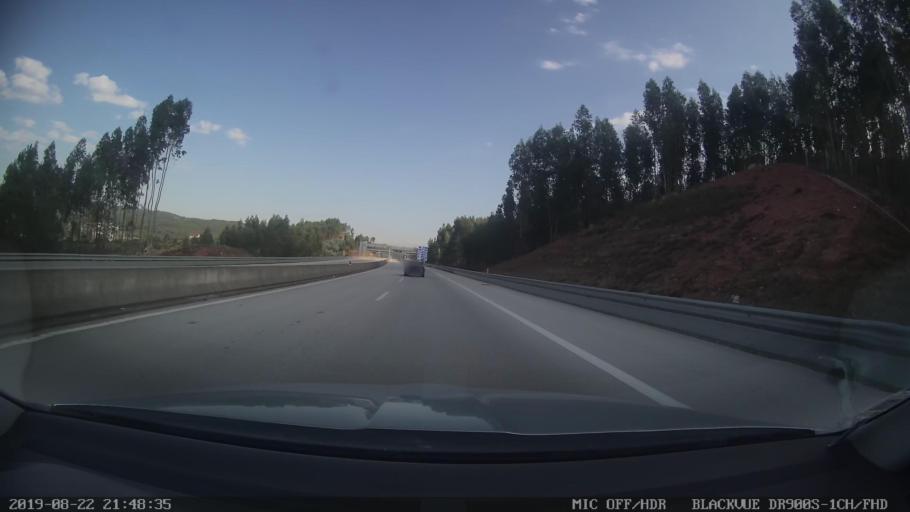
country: PT
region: Coimbra
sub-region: Penela
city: Penela
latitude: 40.0283
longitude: -8.3685
